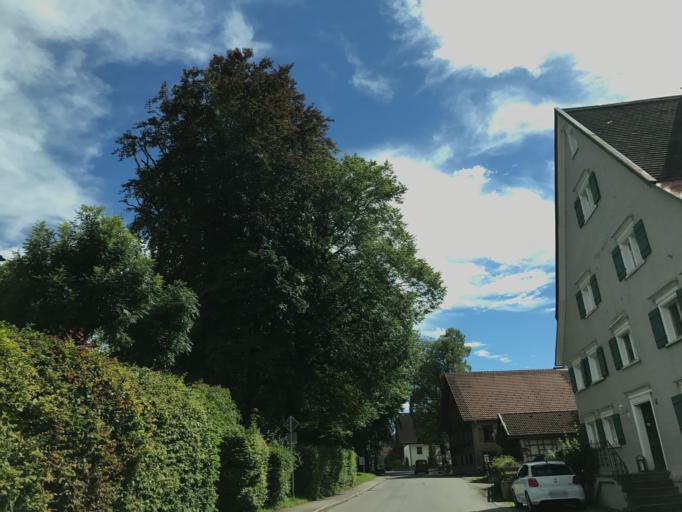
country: DE
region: Bavaria
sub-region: Swabia
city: Rothenbach
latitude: 47.6019
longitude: 9.9585
